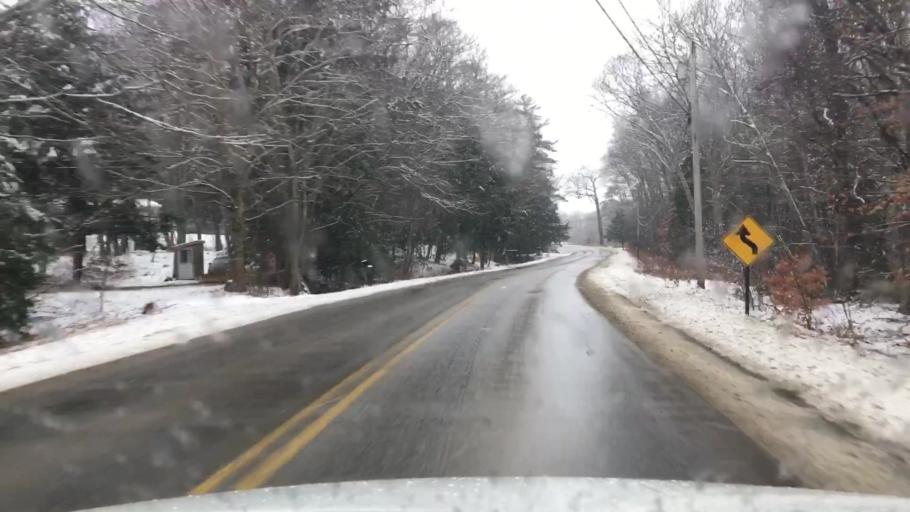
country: US
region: Maine
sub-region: Knox County
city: Warren
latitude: 44.1527
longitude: -69.2828
